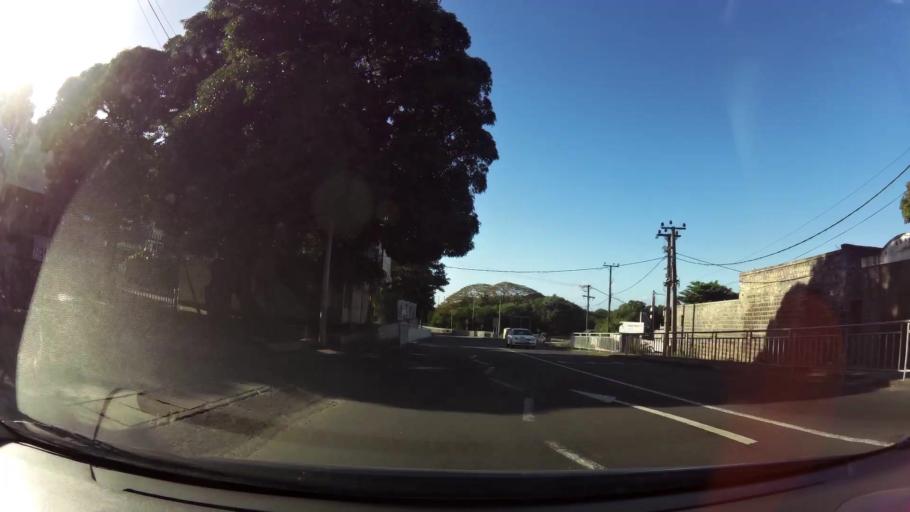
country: MU
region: Moka
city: Pailles
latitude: -20.1774
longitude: 57.4707
